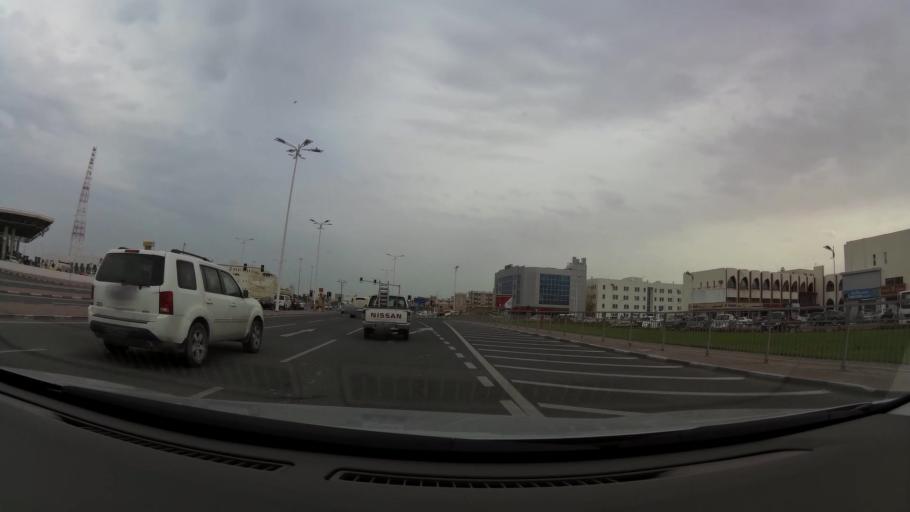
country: QA
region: Baladiyat ad Dawhah
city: Doha
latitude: 25.3117
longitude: 51.4960
